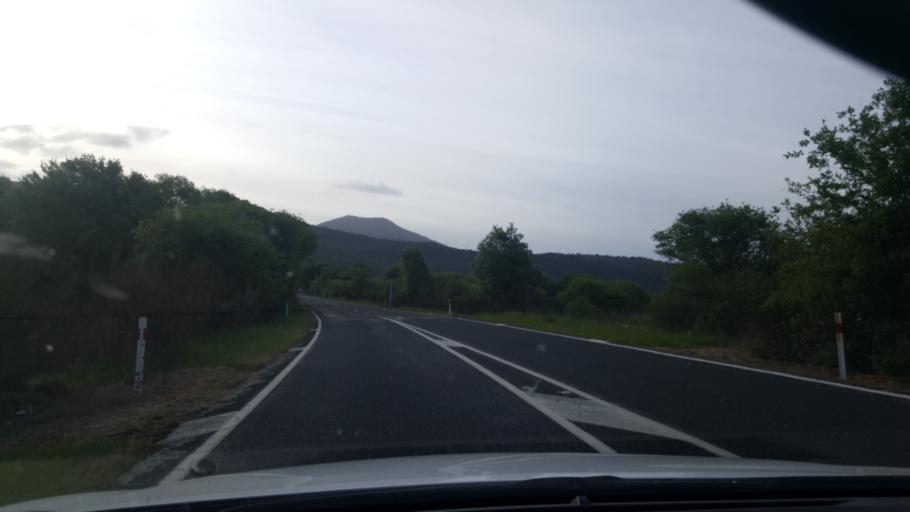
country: NZ
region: Waikato
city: Turangi
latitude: -38.9601
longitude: 175.7628
